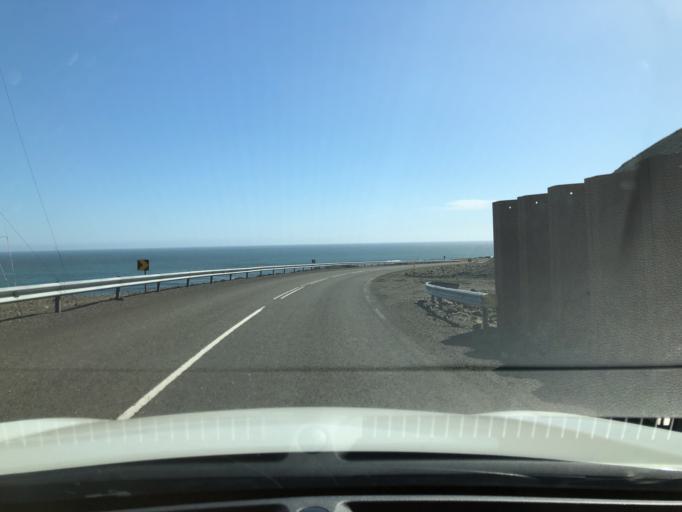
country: IS
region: East
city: Reydarfjoerdur
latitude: 64.4461
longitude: -14.5091
